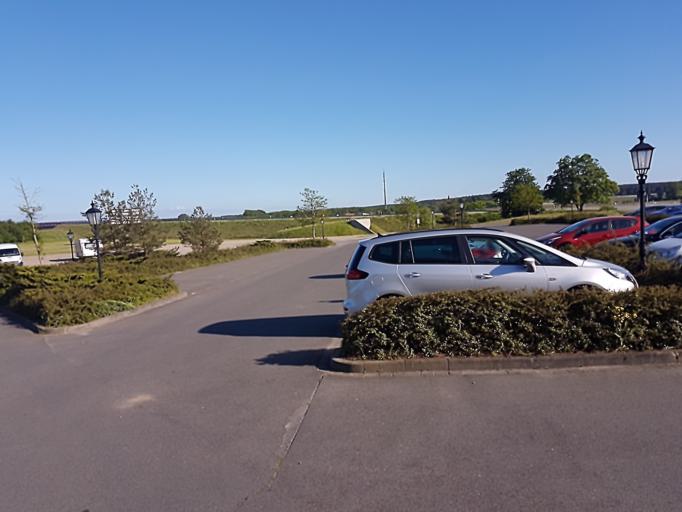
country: DE
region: Mecklenburg-Vorpommern
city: Krakow am See
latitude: 53.6182
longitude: 12.3722
